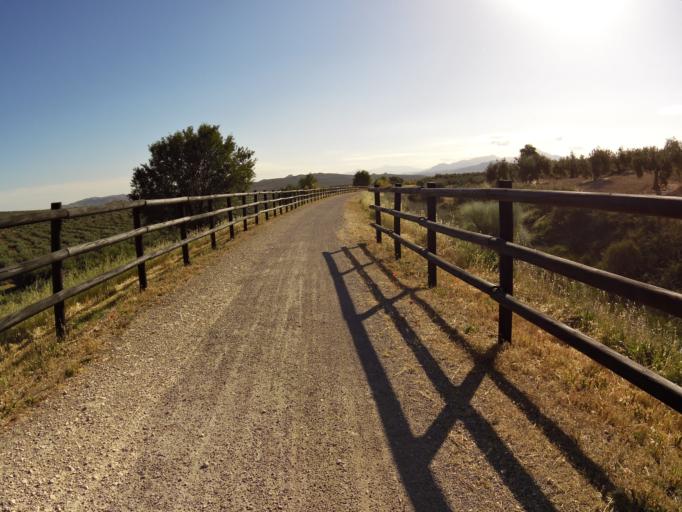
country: ES
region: Andalusia
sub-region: Province of Cordoba
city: Luque
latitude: 37.5704
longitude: -4.2336
